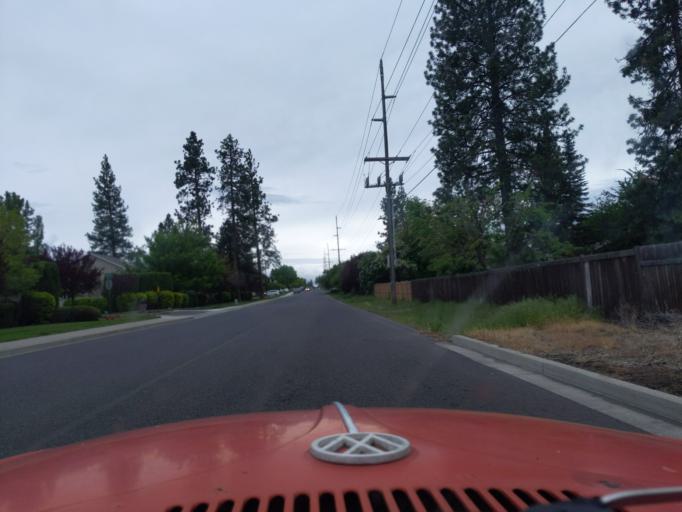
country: US
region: Washington
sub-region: Spokane County
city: Spokane
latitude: 47.6054
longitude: -117.3791
